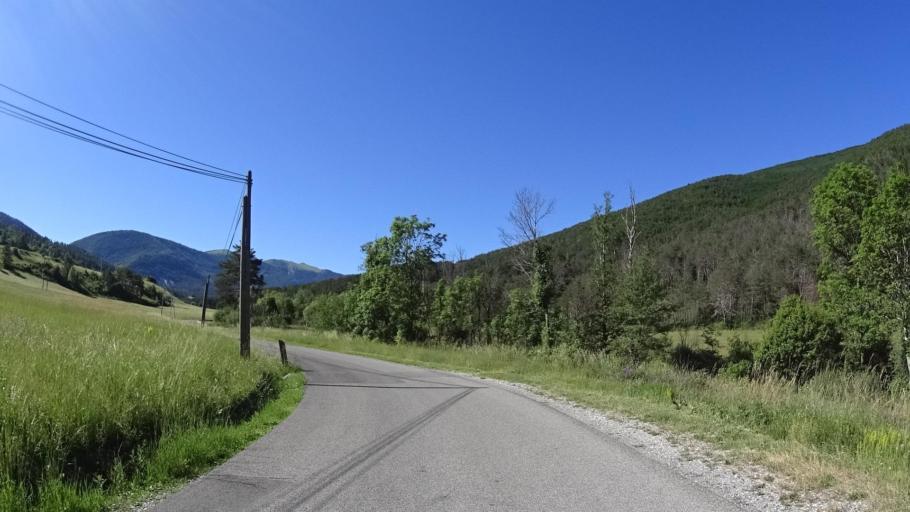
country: FR
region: Provence-Alpes-Cote d'Azur
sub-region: Departement des Alpes-de-Haute-Provence
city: Annot
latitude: 43.9972
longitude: 6.5746
